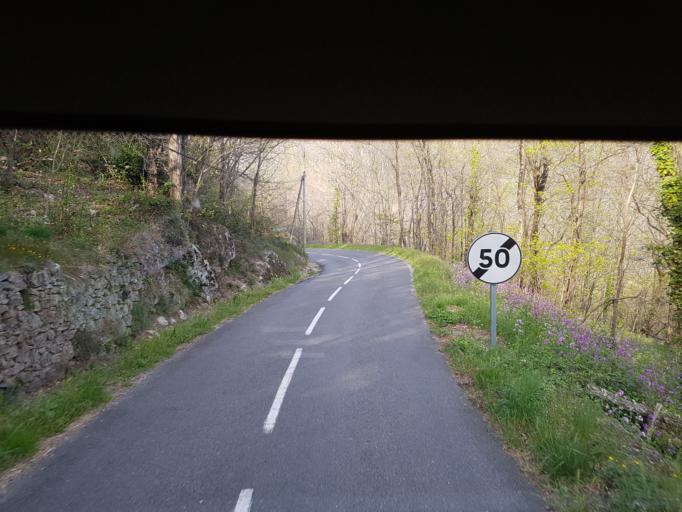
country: FR
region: Languedoc-Roussillon
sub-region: Departement du Gard
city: Branoux-les-Taillades
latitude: 44.3338
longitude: 3.9055
